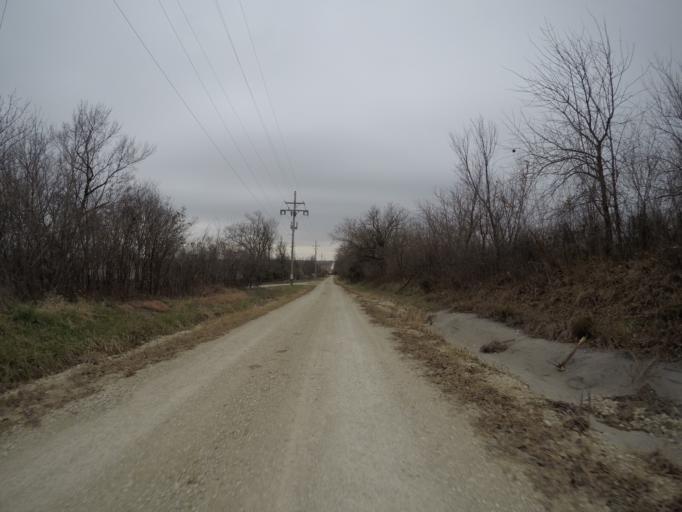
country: US
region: Kansas
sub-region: Wabaunsee County
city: Alma
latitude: 38.8599
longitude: -96.1134
